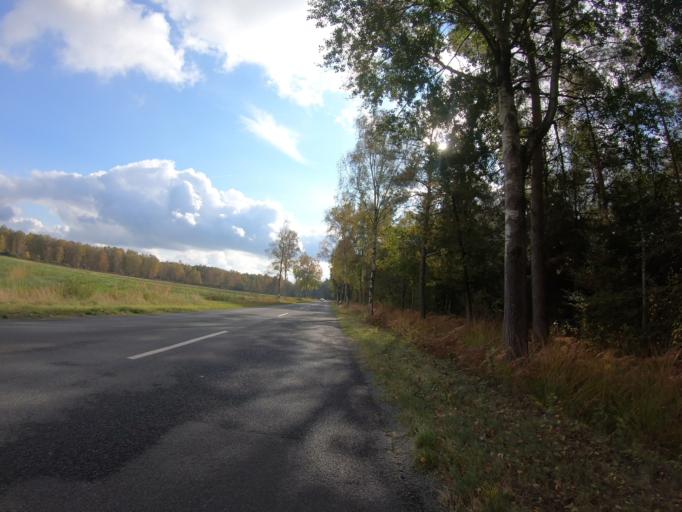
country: DE
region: Lower Saxony
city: Schoneworde
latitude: 52.5922
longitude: 10.6433
